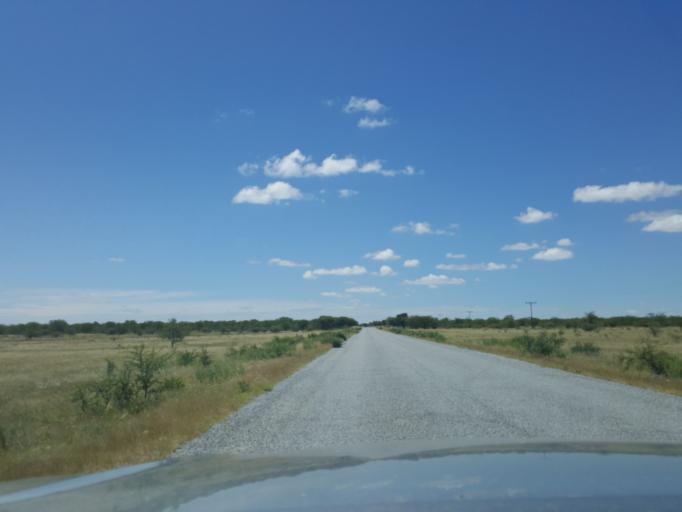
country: BW
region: Central
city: Nata
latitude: -20.1460
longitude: 25.7252
